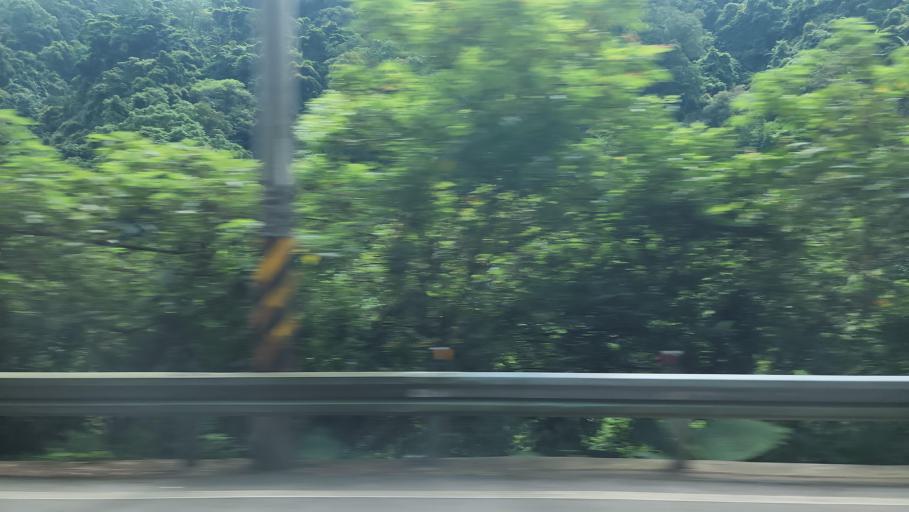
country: TW
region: Taiwan
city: Daxi
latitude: 24.8831
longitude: 121.3784
